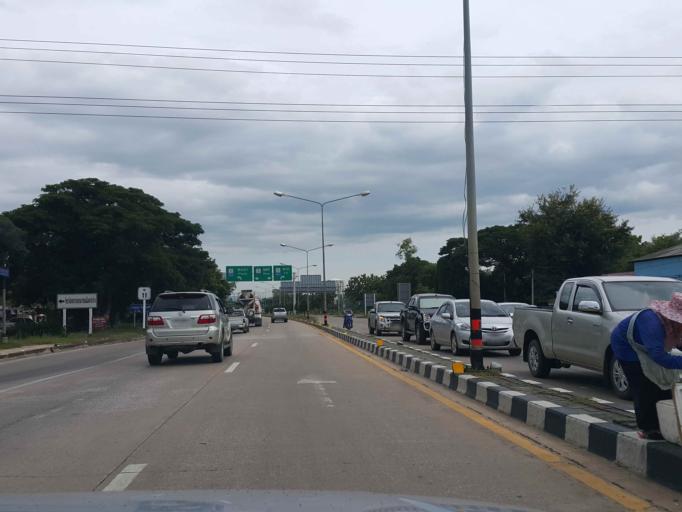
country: TH
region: Lampang
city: Lampang
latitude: 18.2669
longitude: 99.4657
